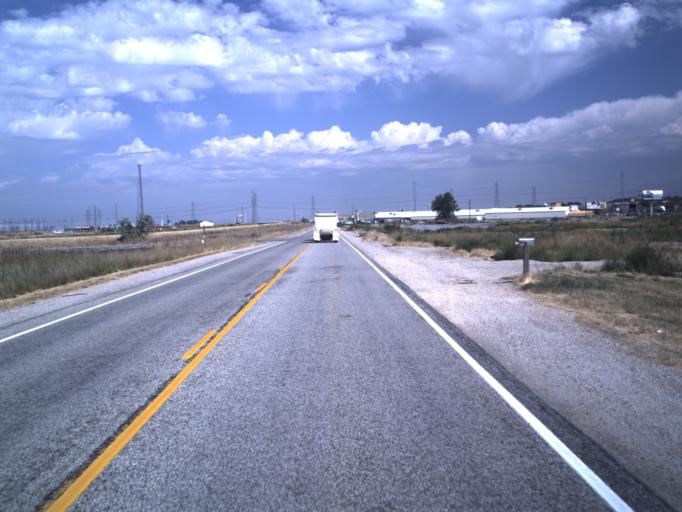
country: US
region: Utah
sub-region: Weber County
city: Farr West
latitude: 41.3285
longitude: -112.0335
